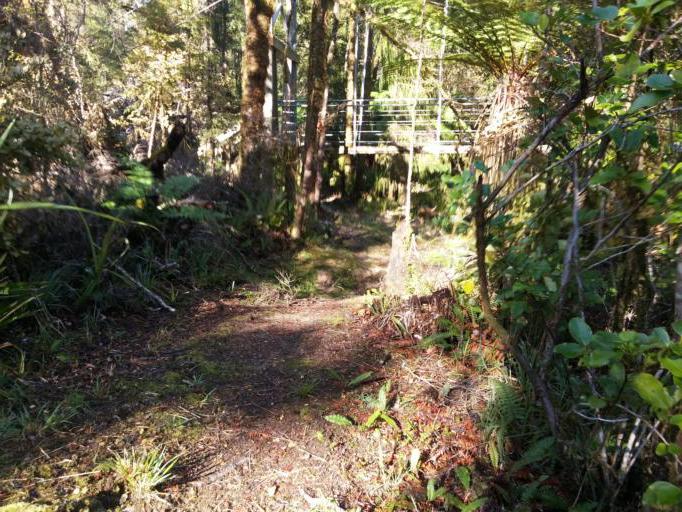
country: NZ
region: West Coast
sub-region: Grey District
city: Greymouth
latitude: -42.1199
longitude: 171.3724
